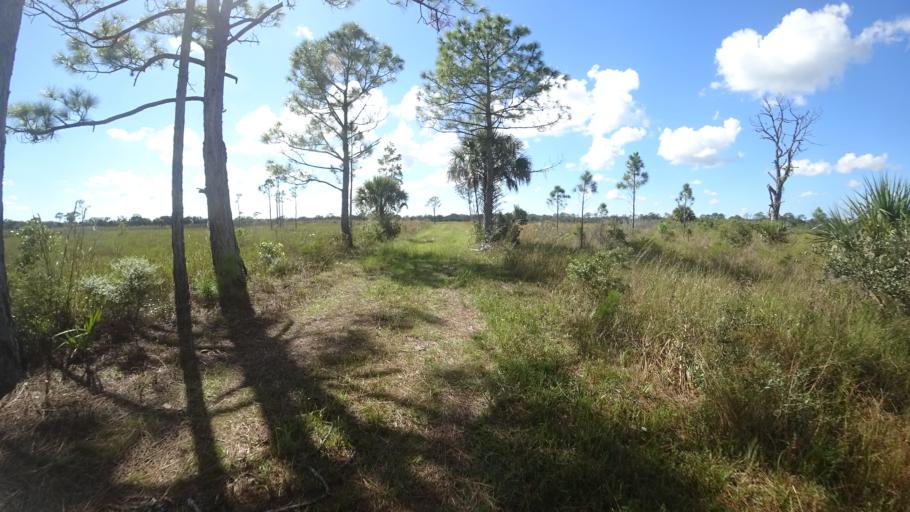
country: US
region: Florida
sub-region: Sarasota County
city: Lake Sarasota
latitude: 27.2620
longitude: -82.2710
